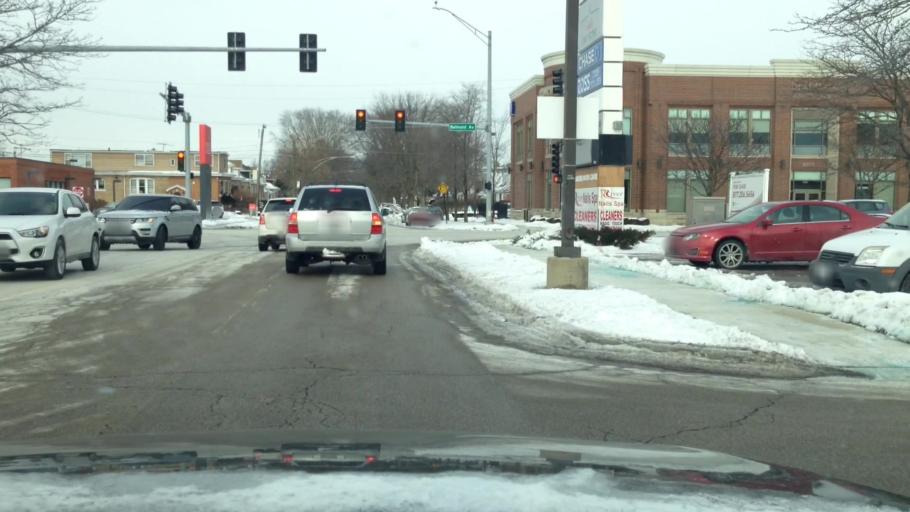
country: US
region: Illinois
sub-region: Cook County
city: River Grove
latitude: 41.9372
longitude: -87.8337
